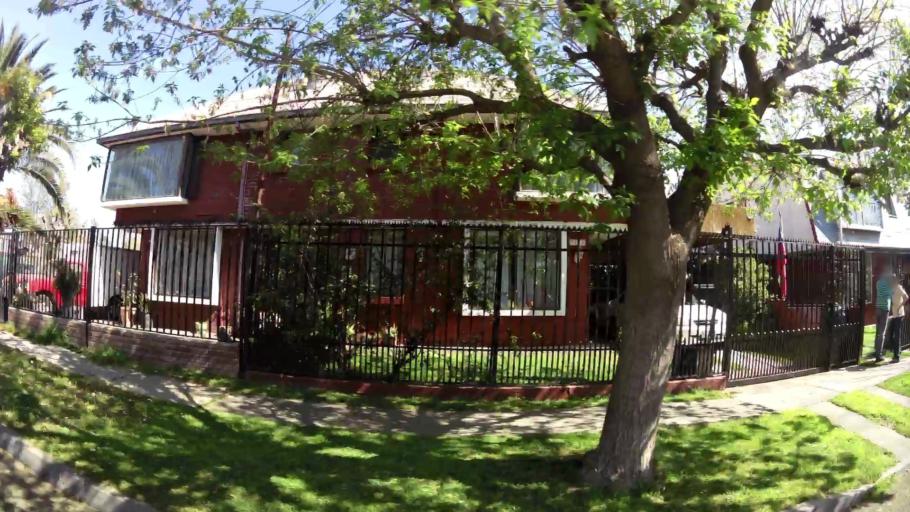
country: CL
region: Santiago Metropolitan
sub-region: Provincia de Santiago
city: Villa Presidente Frei, Nunoa, Santiago, Chile
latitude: -33.4963
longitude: -70.5770
